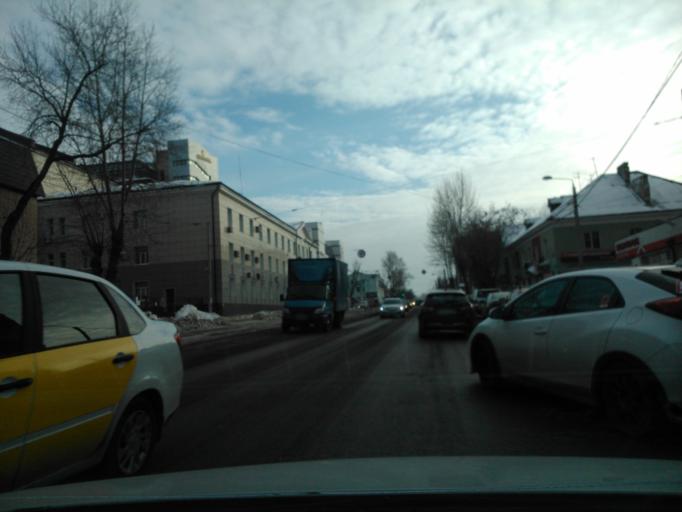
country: RU
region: Perm
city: Perm
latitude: 57.9996
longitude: 56.2414
